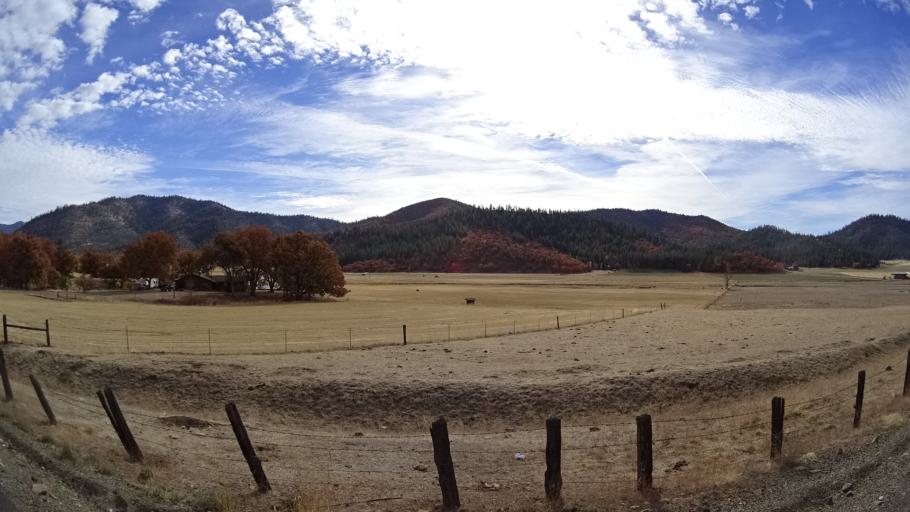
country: US
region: California
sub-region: Siskiyou County
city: Yreka
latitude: 41.6269
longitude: -122.7763
